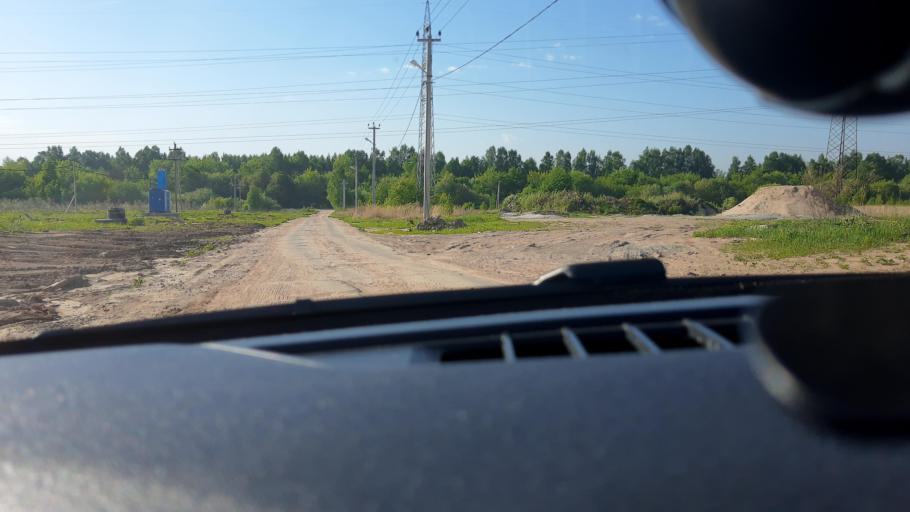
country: RU
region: Nizjnij Novgorod
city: Burevestnik
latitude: 56.1774
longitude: 43.8976
